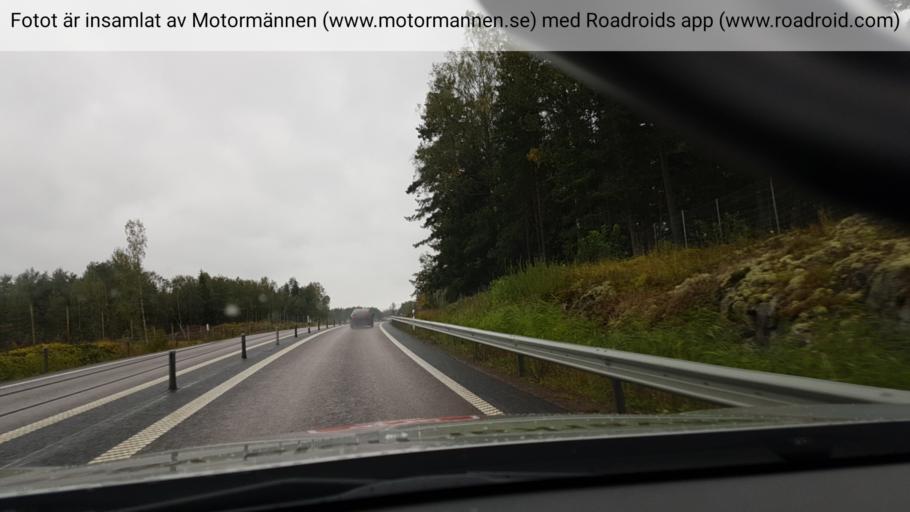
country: SE
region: Vaestra Goetaland
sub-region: Amals Kommun
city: Amal
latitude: 58.9312
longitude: 12.5973
